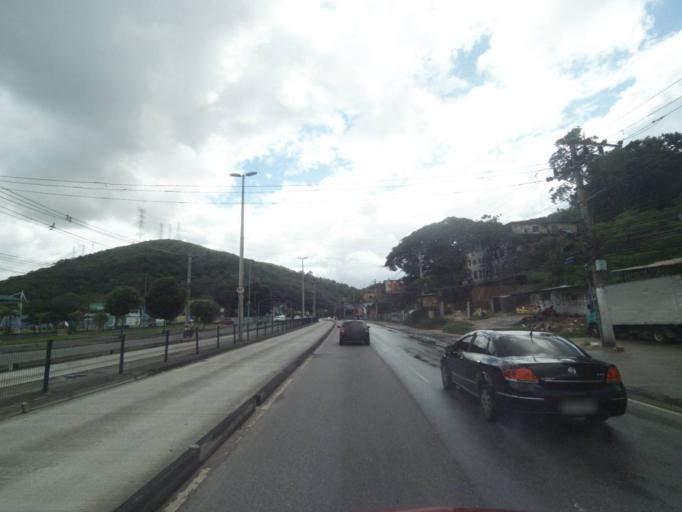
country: BR
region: Rio de Janeiro
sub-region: Sao Joao De Meriti
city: Sao Joao de Meriti
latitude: -22.9141
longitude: -43.3605
